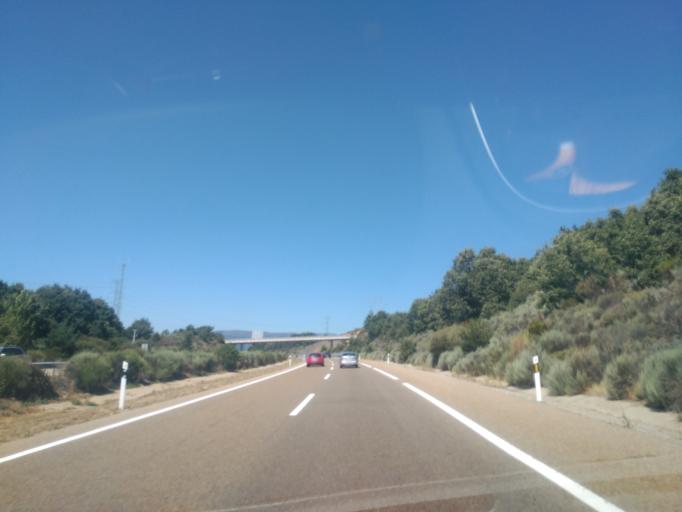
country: ES
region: Castille and Leon
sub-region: Provincia de Zamora
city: Palacios de Sanabria
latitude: 42.0554
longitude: -6.5627
